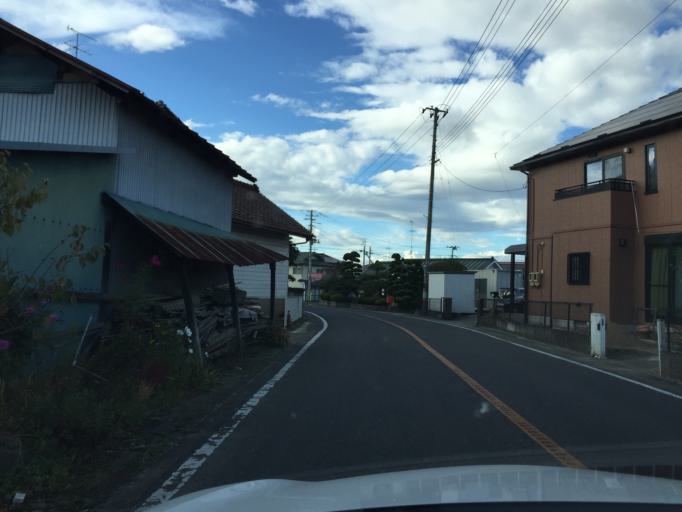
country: JP
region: Fukushima
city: Sukagawa
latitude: 37.2693
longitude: 140.4113
